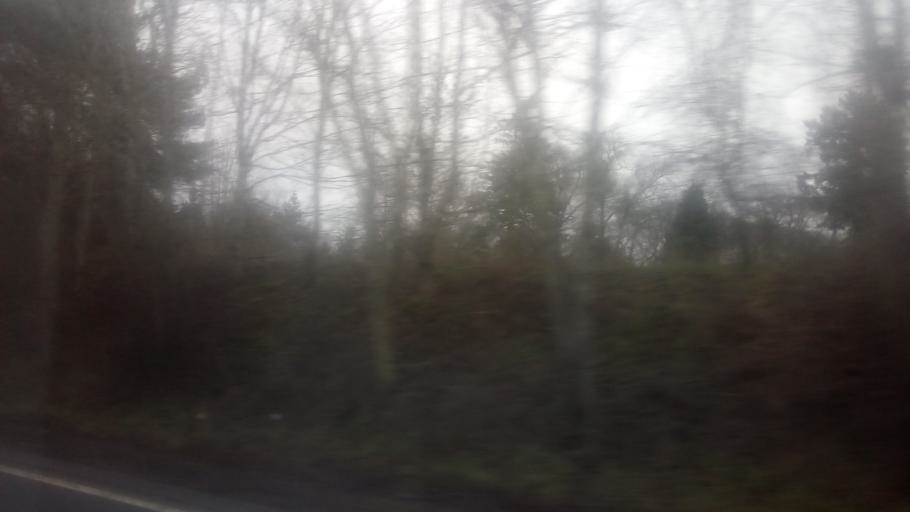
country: GB
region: Scotland
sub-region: The Scottish Borders
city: Newtown St Boswells
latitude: 55.5993
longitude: -2.6719
